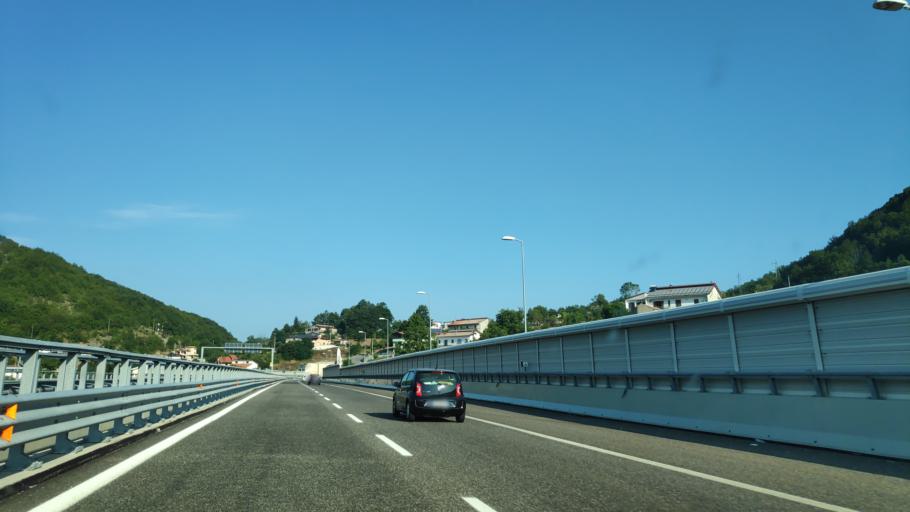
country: IT
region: Basilicate
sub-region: Provincia di Potenza
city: Lauria
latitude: 40.0195
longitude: 15.8844
